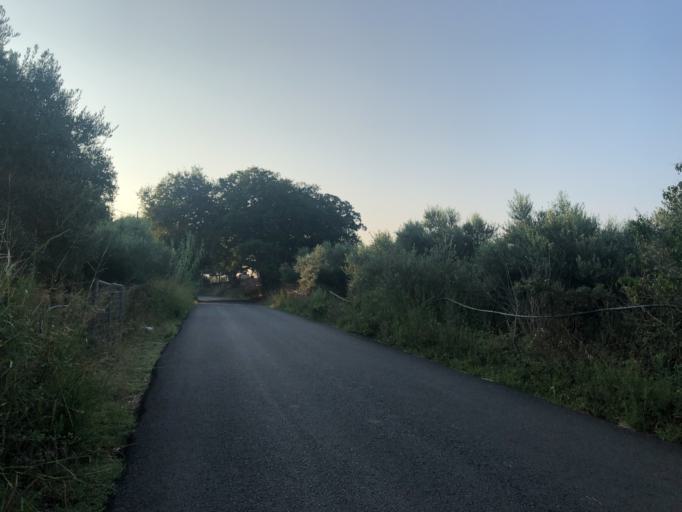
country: GR
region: Crete
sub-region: Nomos Chanias
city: Georgioupolis
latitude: 35.3500
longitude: 24.2798
